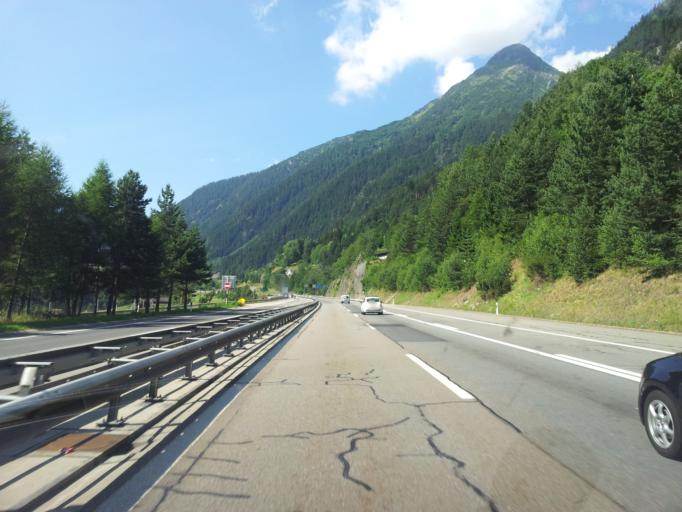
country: CH
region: Uri
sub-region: Uri
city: Andermatt
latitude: 46.7039
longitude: 8.5996
